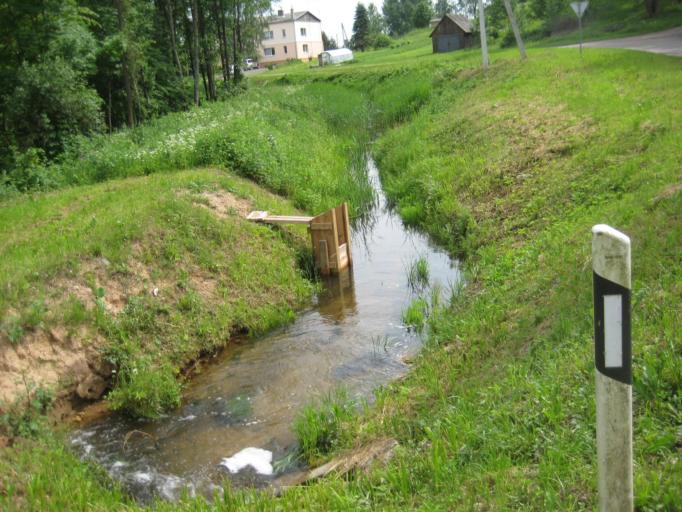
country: LT
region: Utenos apskritis
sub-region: Utena
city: Utena
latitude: 55.6952
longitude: 25.8013
